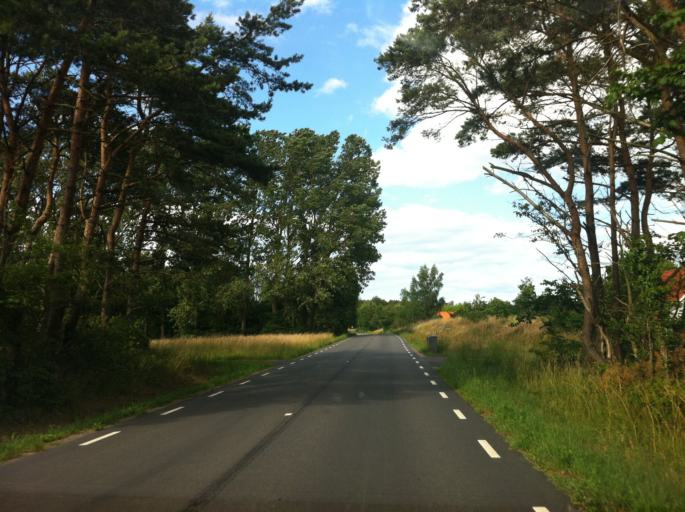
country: SE
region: Skane
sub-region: Simrishamns Kommun
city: Simrishamn
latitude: 55.4438
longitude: 14.2428
